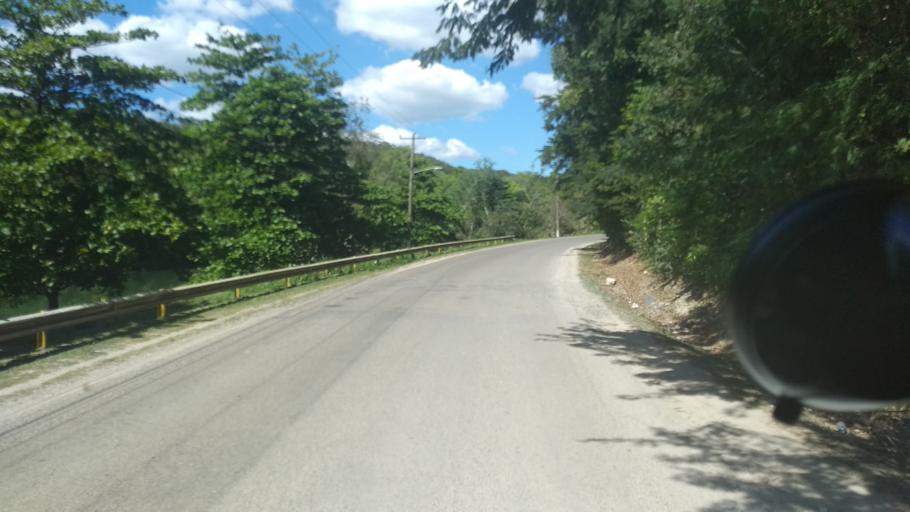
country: BZ
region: Cayo
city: Benque Viejo del Carmen
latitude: 17.0813
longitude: -89.1363
